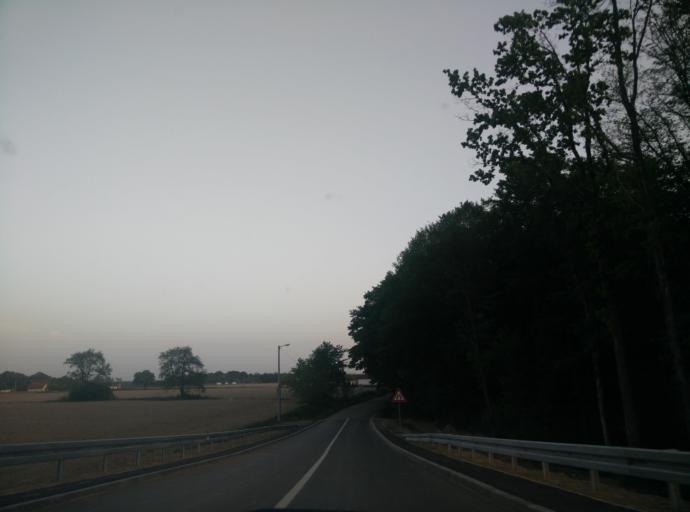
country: BA
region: Brcko
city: Brcko
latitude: 44.8310
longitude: 18.8378
